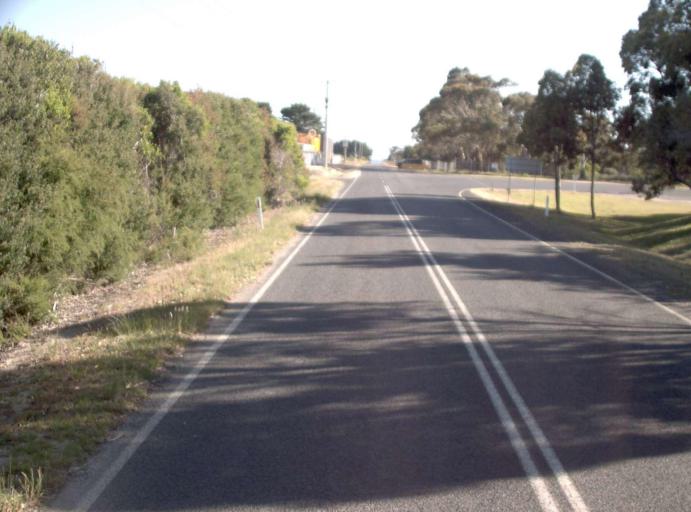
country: AU
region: Victoria
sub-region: Latrobe
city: Morwell
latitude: -38.7096
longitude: 146.3969
